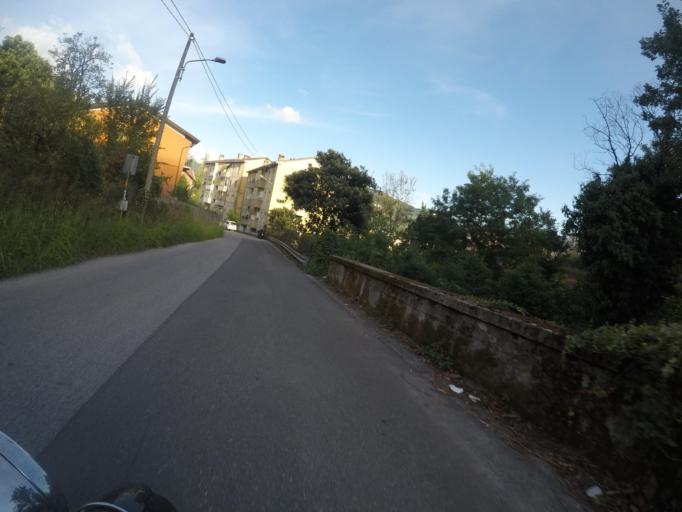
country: IT
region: Tuscany
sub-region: Provincia di Massa-Carrara
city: Carrara
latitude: 44.0821
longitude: 10.0929
